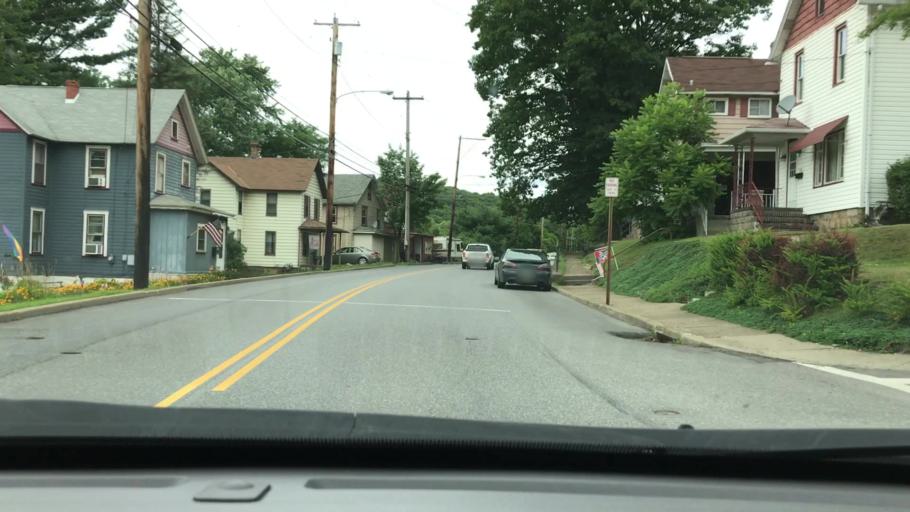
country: US
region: Pennsylvania
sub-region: Elk County
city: Ridgway
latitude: 41.4307
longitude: -78.7343
